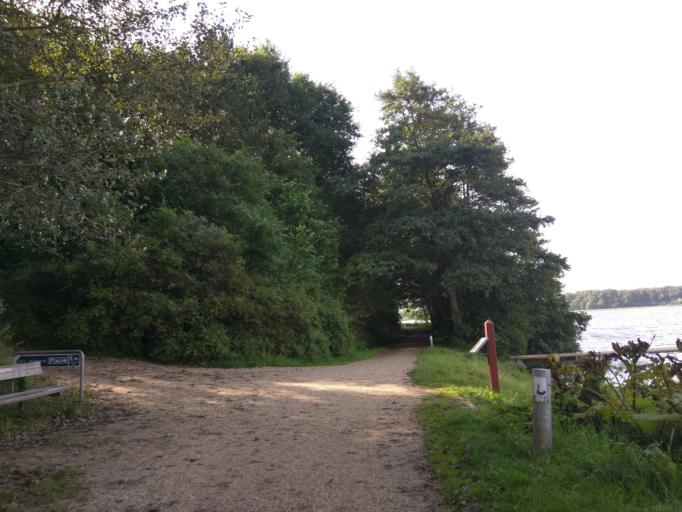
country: DK
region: Central Jutland
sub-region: Viborg Kommune
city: Viborg
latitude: 56.4390
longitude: 9.4183
